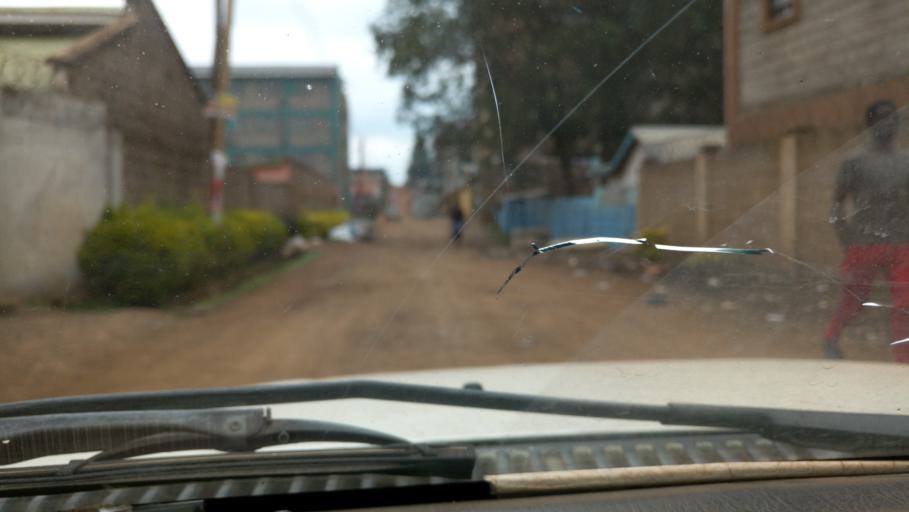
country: KE
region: Kiambu
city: Kikuyu
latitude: -1.2820
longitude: 36.7283
